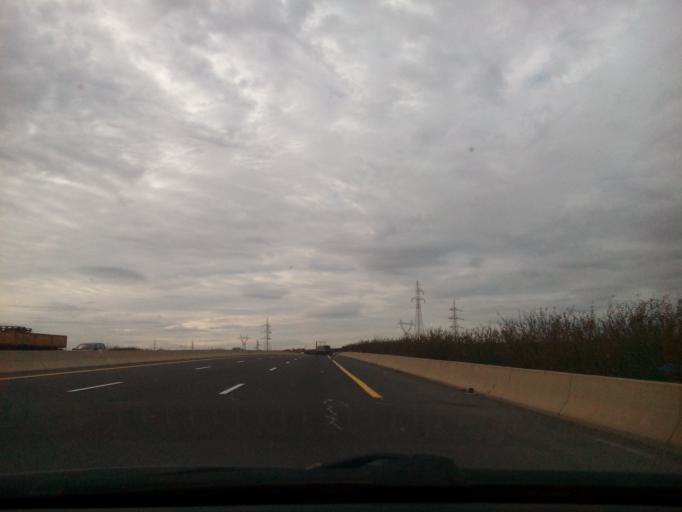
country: DZ
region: Mascara
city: Sig
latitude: 35.5424
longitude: -0.3691
